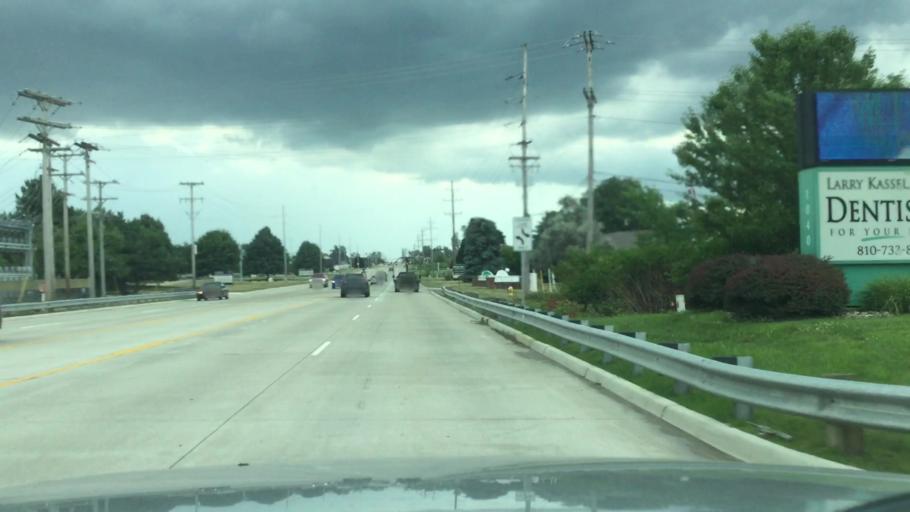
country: US
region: Michigan
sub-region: Genesee County
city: Swartz Creek
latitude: 43.0155
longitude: -83.7731
